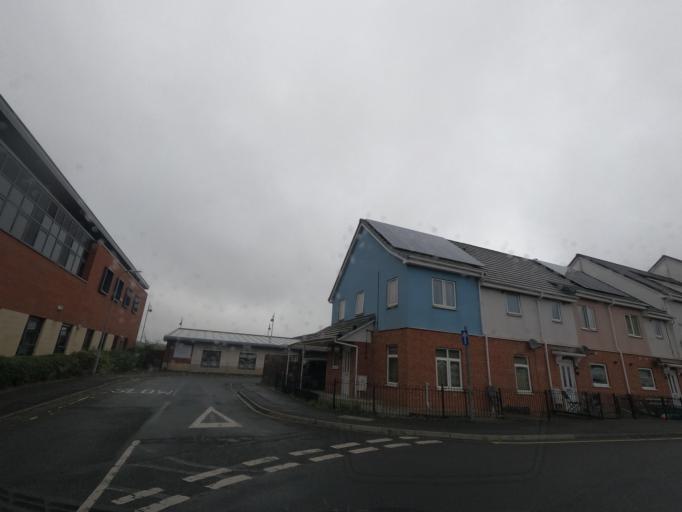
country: GB
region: England
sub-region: Middlesbrough
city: Middlesbrough
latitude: 54.5719
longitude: -1.2151
